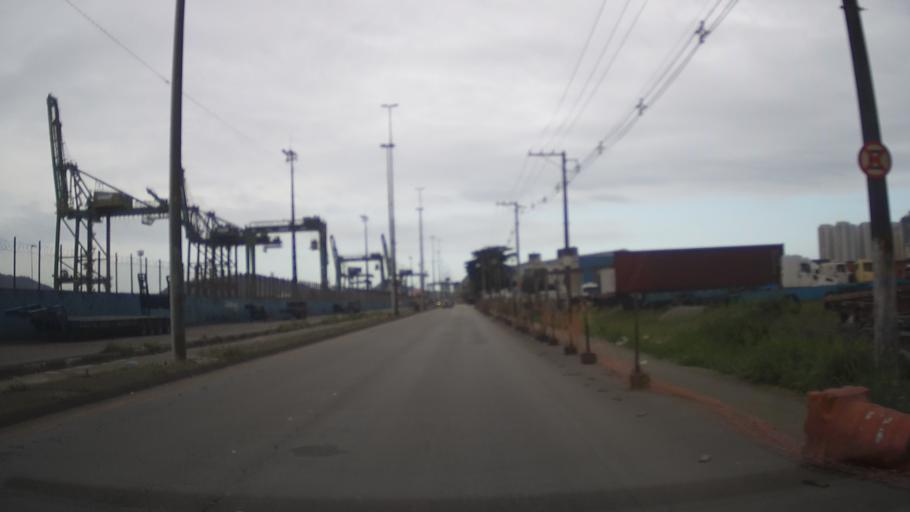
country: BR
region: Sao Paulo
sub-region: Santos
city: Santos
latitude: -23.9711
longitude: -46.2981
